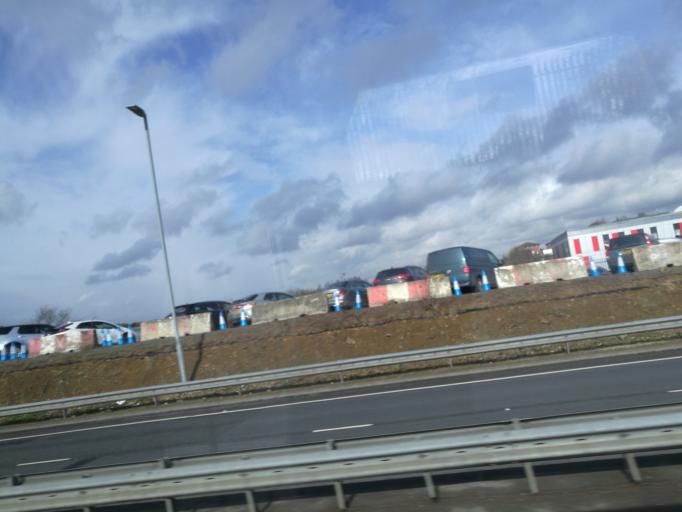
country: GB
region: England
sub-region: Luton
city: Luton
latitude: 51.8753
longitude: -0.3824
